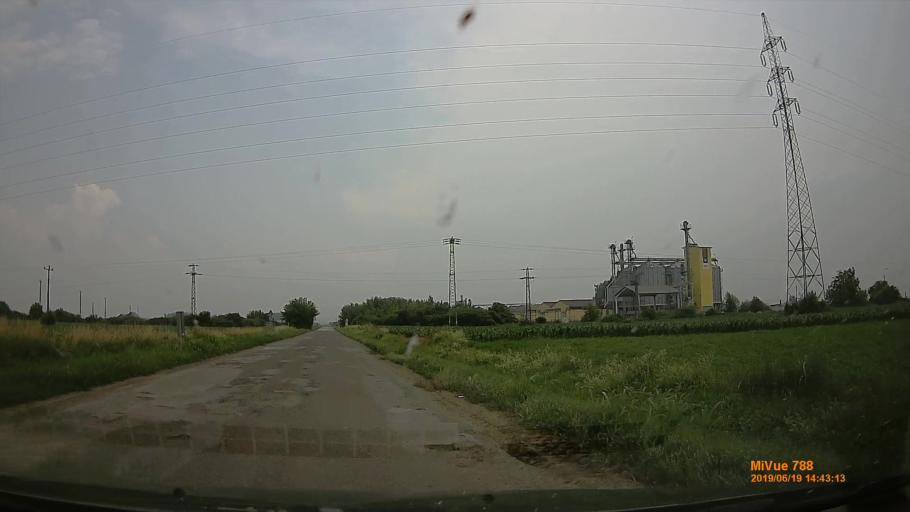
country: HU
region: Baranya
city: Szigetvar
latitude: 46.0414
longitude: 17.8177
